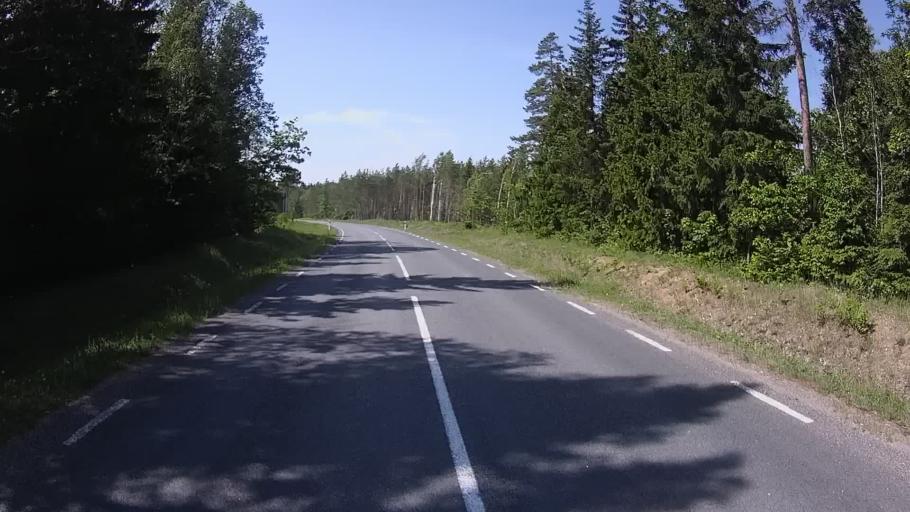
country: EE
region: Saare
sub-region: Kuressaare linn
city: Kuressaare
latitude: 58.5180
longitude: 22.3912
